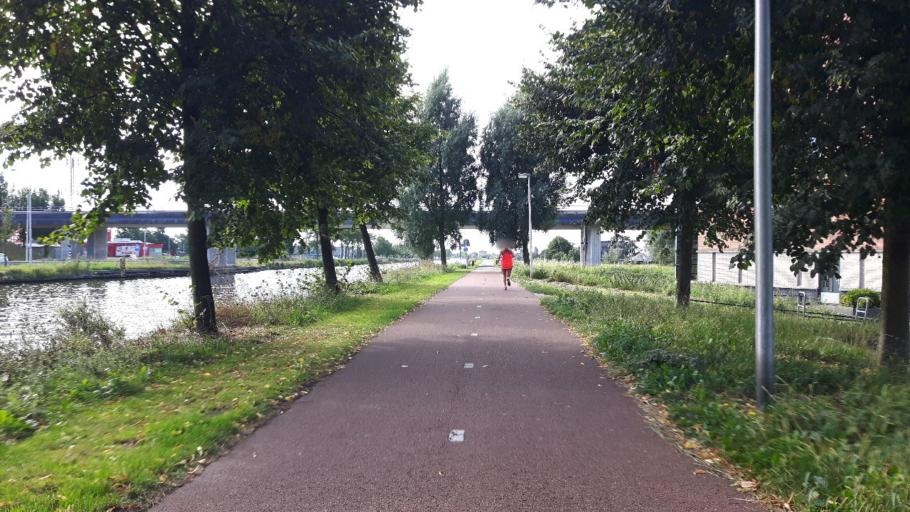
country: NL
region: North Holland
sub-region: Gemeente Purmerend
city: Purmerend
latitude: 52.4885
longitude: 4.9491
